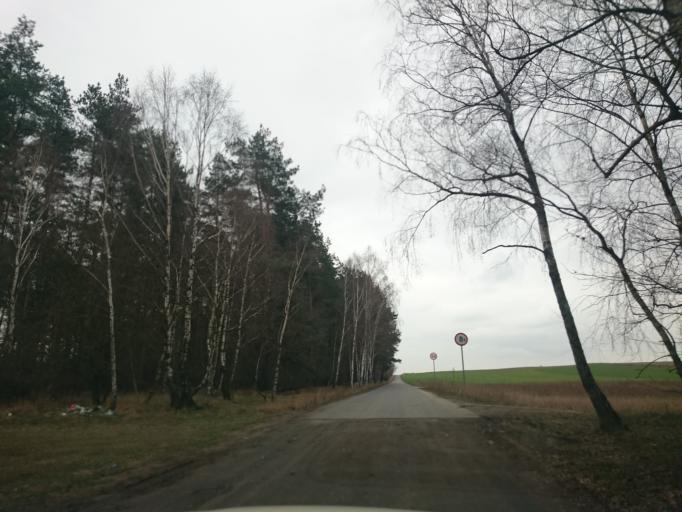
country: PL
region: Kujawsko-Pomorskie
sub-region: Powiat golubsko-dobrzynski
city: Ciechocin
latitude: 53.0488
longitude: 18.8799
